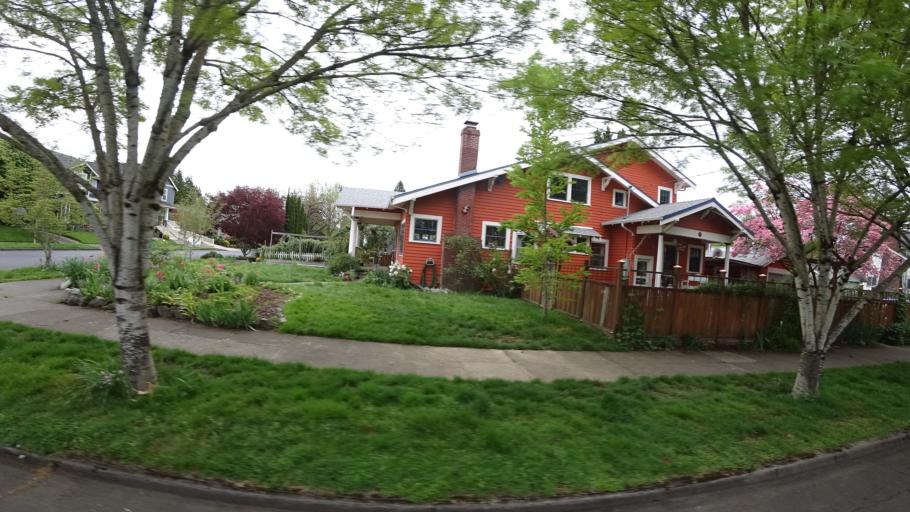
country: US
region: Oregon
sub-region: Clackamas County
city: Milwaukie
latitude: 45.4790
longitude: -122.6461
